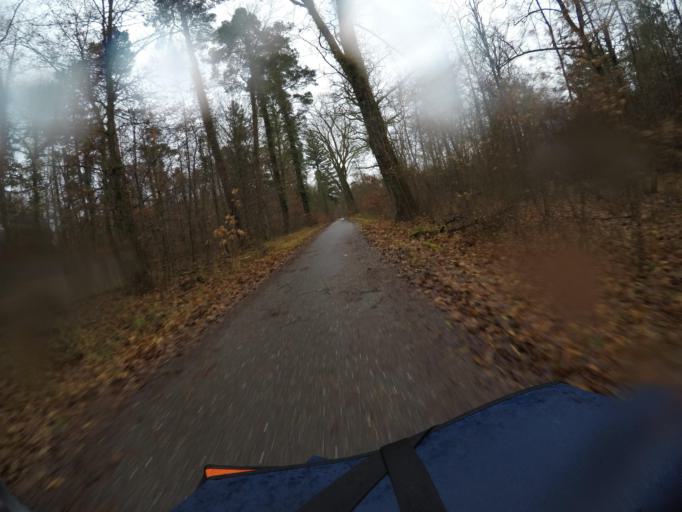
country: DE
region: Baden-Wuerttemberg
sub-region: Karlsruhe Region
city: Eggenstein-Leopoldshafen
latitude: 49.0685
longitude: 8.4455
